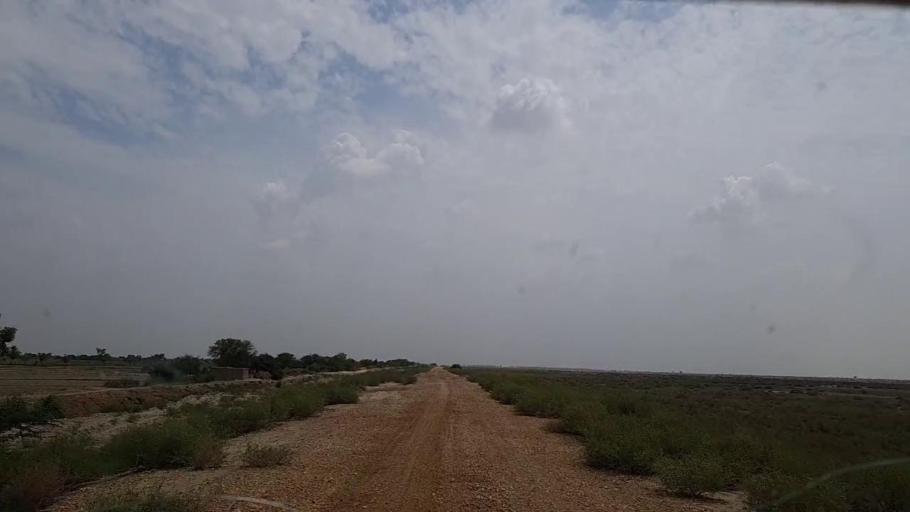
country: PK
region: Sindh
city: Johi
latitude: 26.7967
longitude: 67.6019
